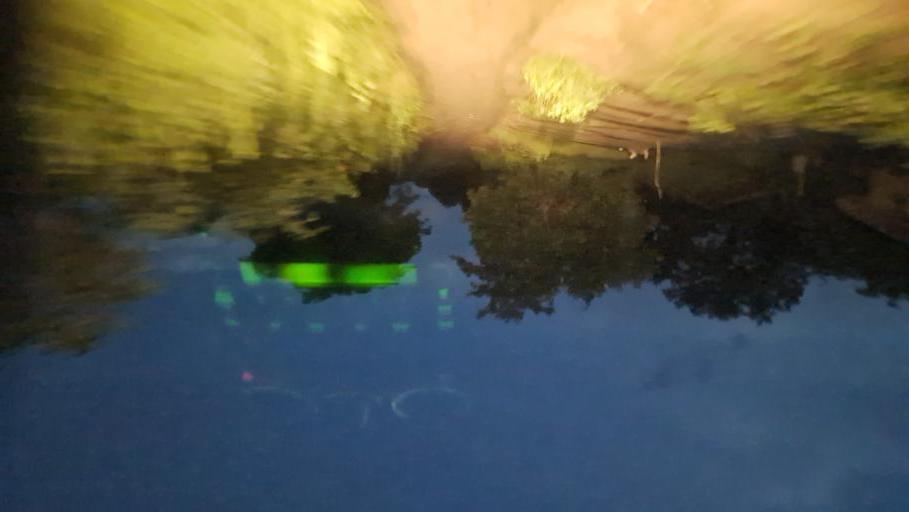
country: MZ
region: Nampula
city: Nampula
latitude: -14.6689
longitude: 39.8357
